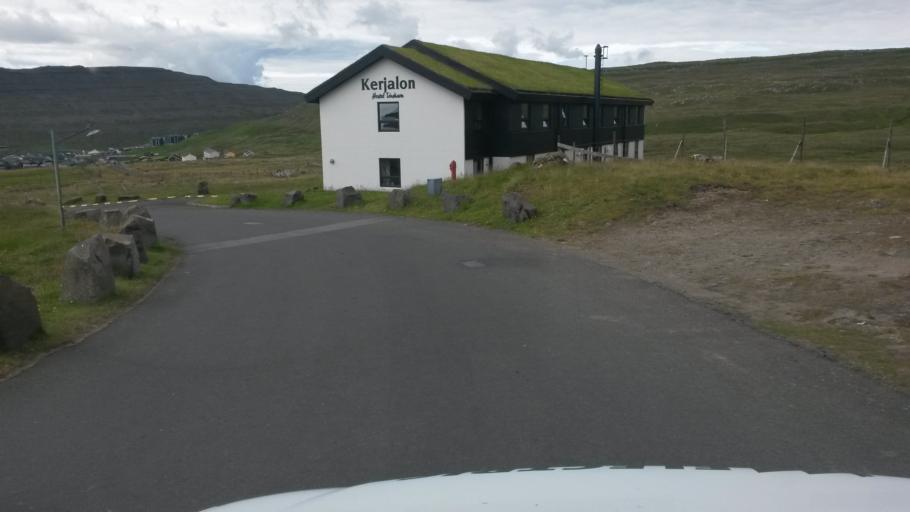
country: FO
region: Streymoy
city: Hoyvik
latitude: 62.0130
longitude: -6.8013
